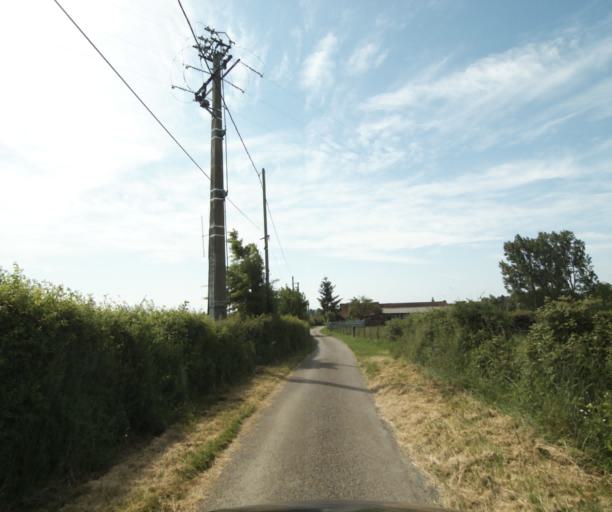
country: FR
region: Bourgogne
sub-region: Departement de Saone-et-Loire
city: Gueugnon
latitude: 46.5439
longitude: 4.1226
